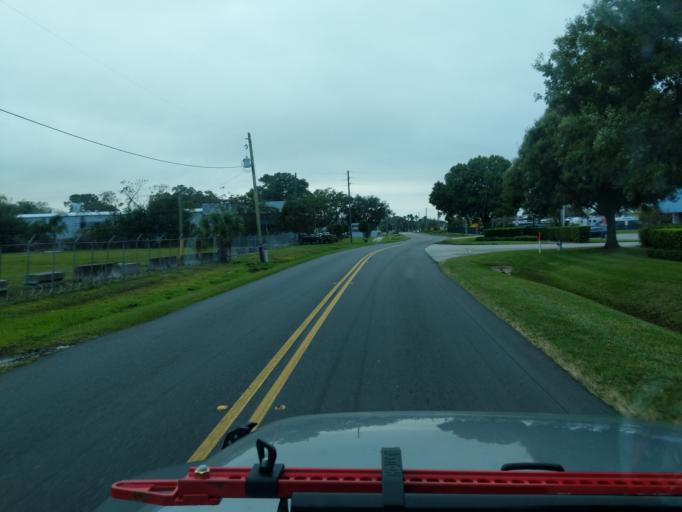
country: US
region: Florida
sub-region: Orange County
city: Winter Garden
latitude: 28.5549
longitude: -81.5647
